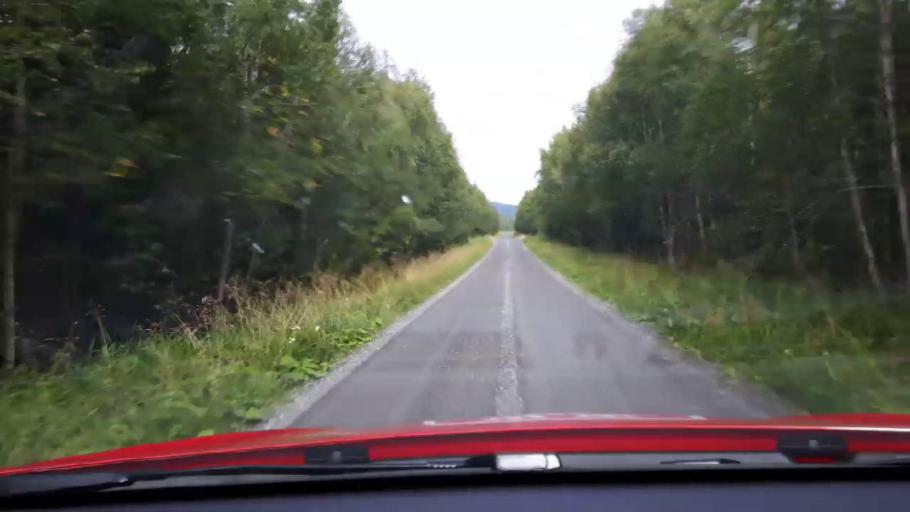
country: SE
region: Jaemtland
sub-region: Are Kommun
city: Are
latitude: 63.7723
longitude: 13.0934
